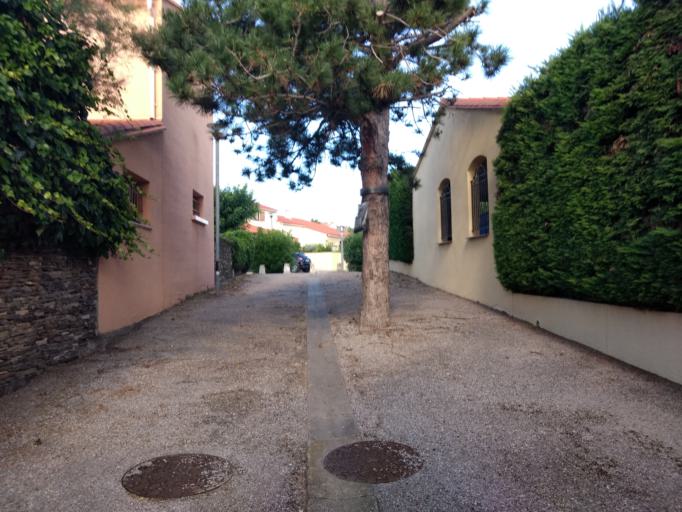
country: FR
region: Languedoc-Roussillon
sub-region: Departement des Pyrenees-Orientales
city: Villeneuve-de-la-Raho
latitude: 42.6390
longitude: 2.9105
